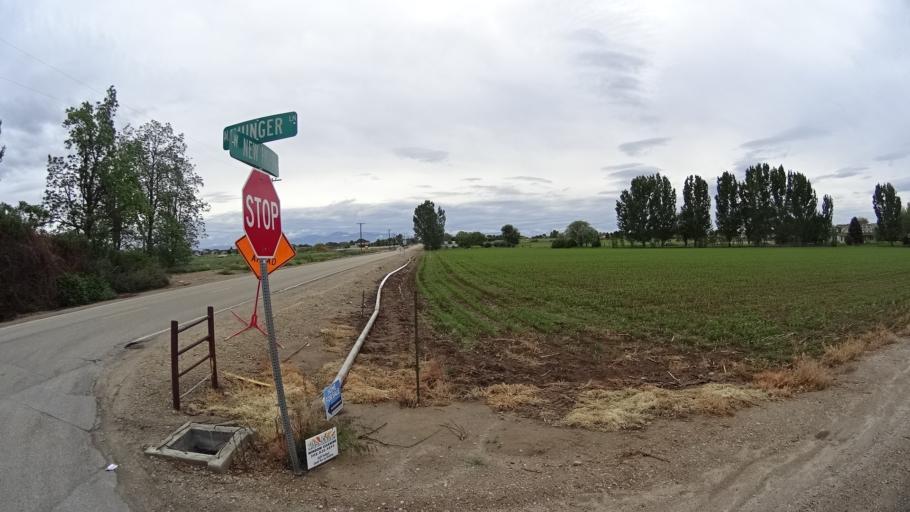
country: US
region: Idaho
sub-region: Ada County
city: Star
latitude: 43.7176
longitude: -116.5032
